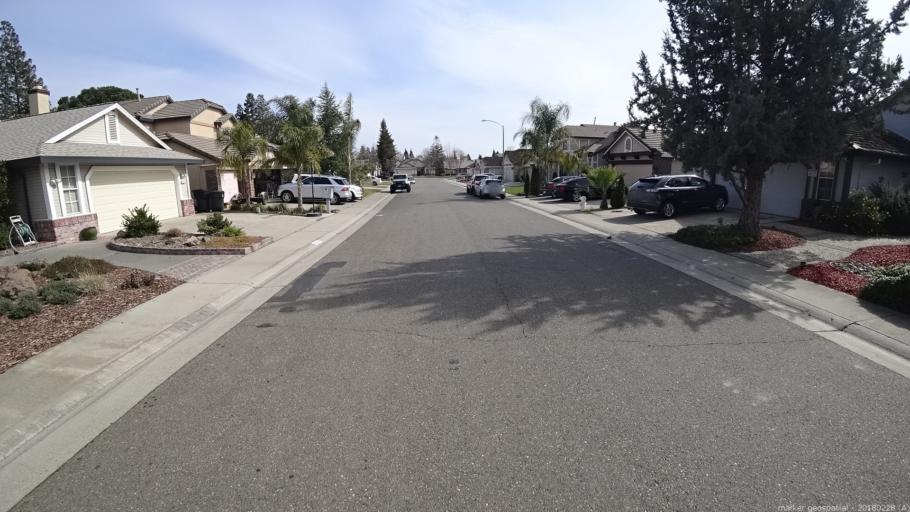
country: US
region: California
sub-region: Sacramento County
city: Antelope
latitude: 38.7205
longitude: -121.3452
